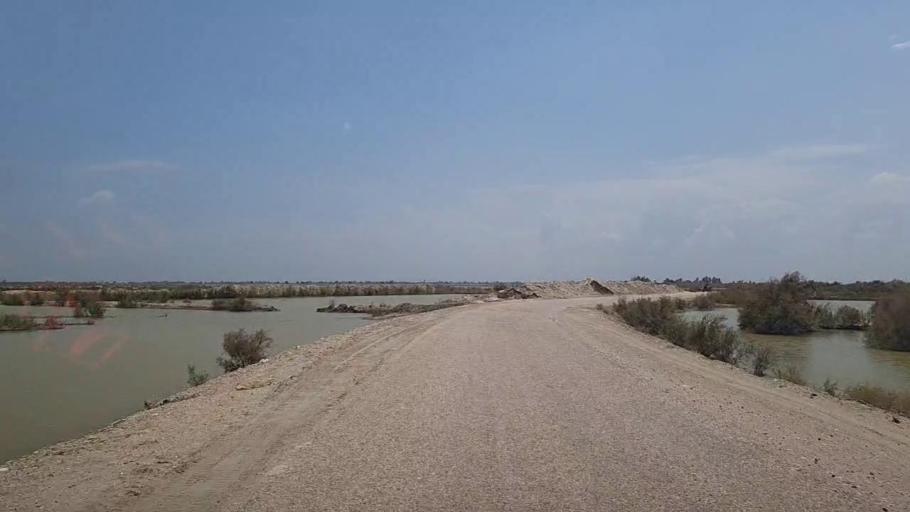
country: PK
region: Sindh
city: Kandhkot
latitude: 28.2875
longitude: 69.1643
